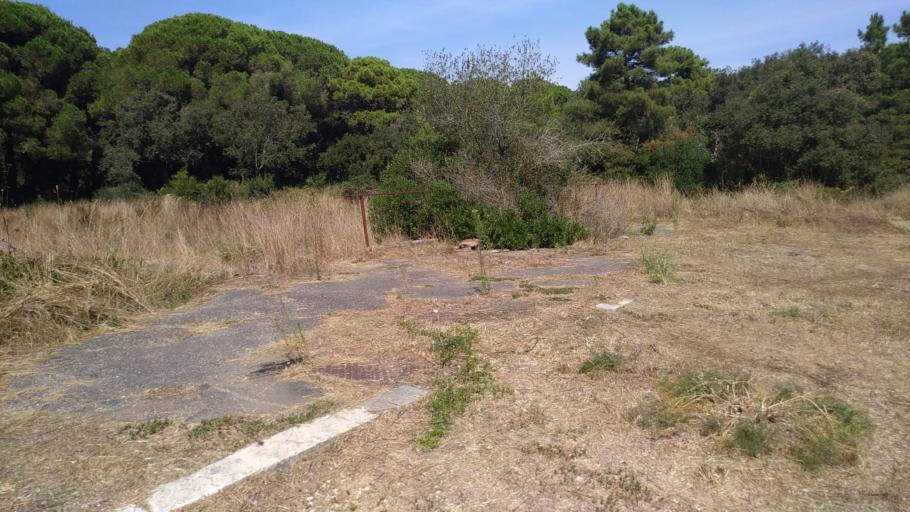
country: IT
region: Latium
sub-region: Citta metropolitana di Roma Capitale
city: Lido di Ostia
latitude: 41.7326
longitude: 12.3039
